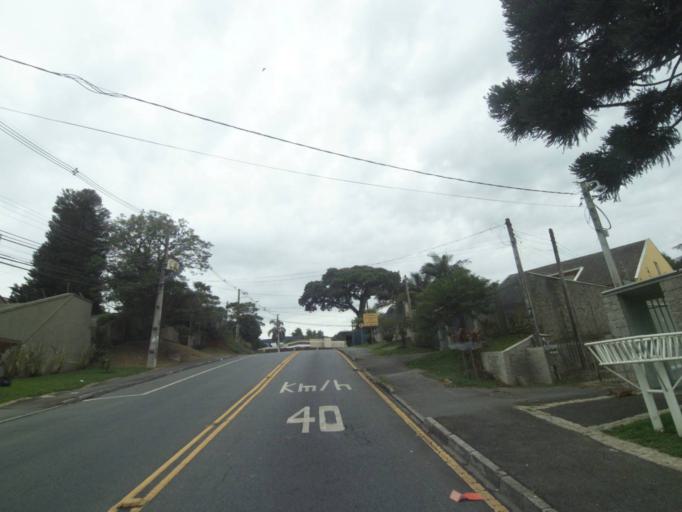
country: BR
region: Parana
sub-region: Curitiba
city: Curitiba
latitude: -25.4036
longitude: -49.2921
